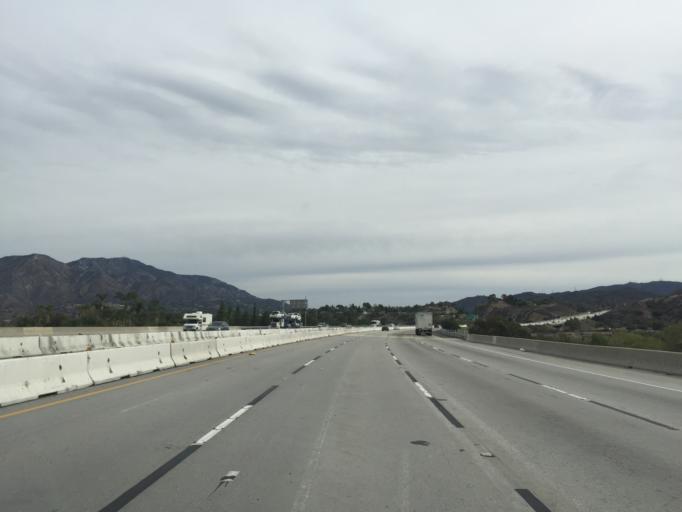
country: US
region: California
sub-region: Los Angeles County
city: Burbank
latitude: 34.2704
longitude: -118.3426
